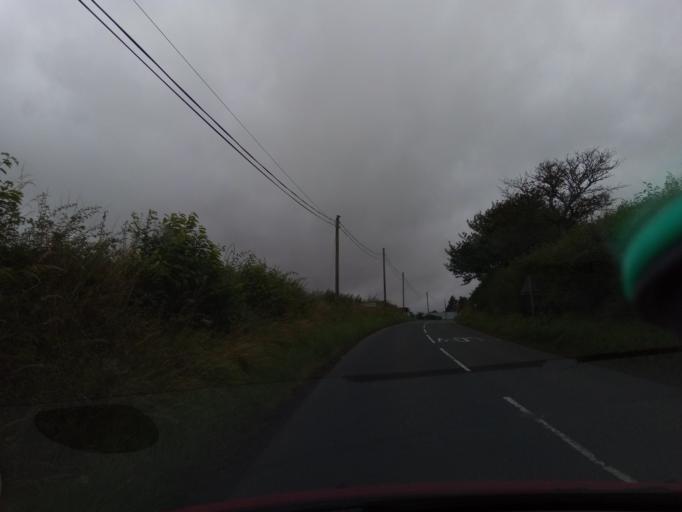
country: GB
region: Scotland
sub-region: The Scottish Borders
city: Kelso
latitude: 55.6270
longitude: -2.4987
